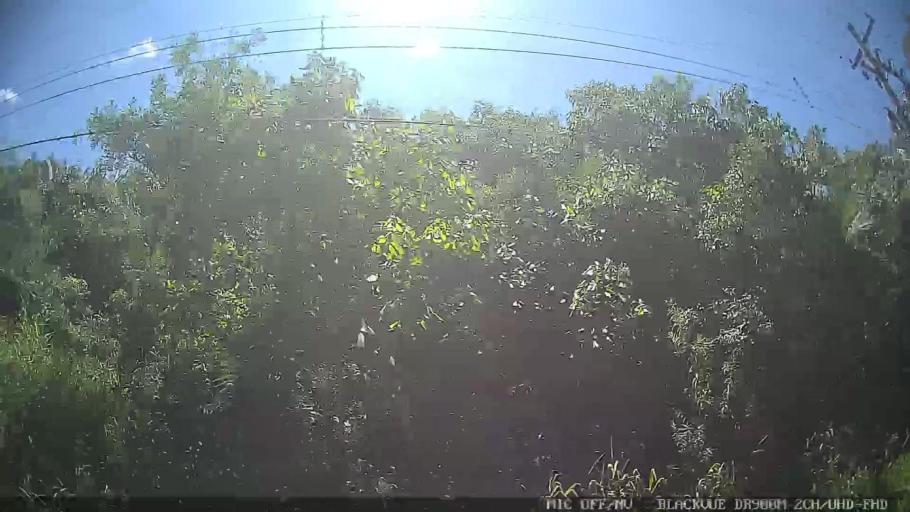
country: BR
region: Sao Paulo
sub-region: Mogi das Cruzes
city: Mogi das Cruzes
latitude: -23.5770
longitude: -46.1487
